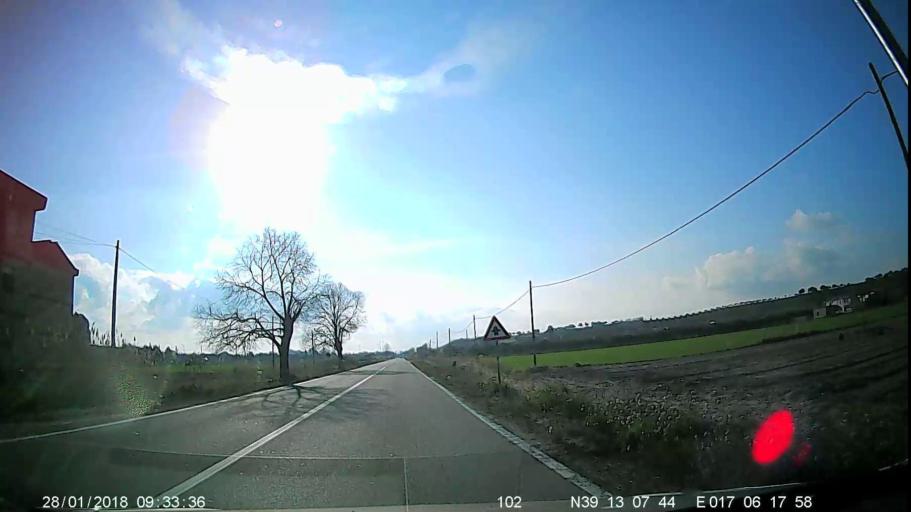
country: IT
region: Calabria
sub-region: Provincia di Crotone
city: Tronca
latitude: 39.2182
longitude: 17.1053
